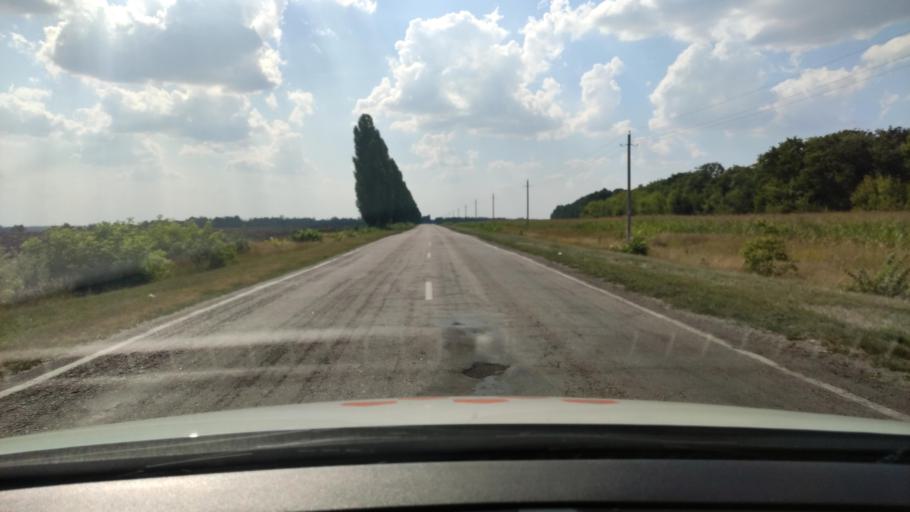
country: RU
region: Voronezj
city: Sadovoye
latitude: 51.7626
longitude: 40.4613
